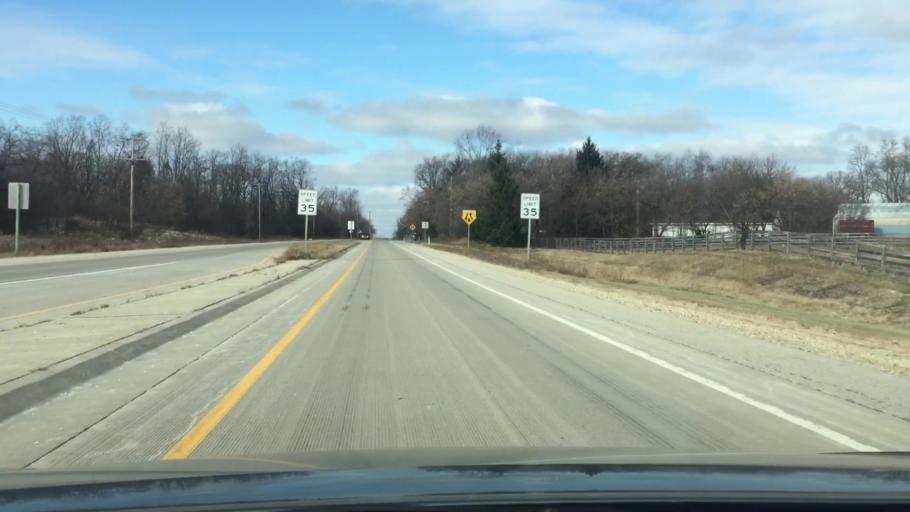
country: US
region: Wisconsin
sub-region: Waukesha County
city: North Prairie
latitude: 42.9498
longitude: -88.3539
